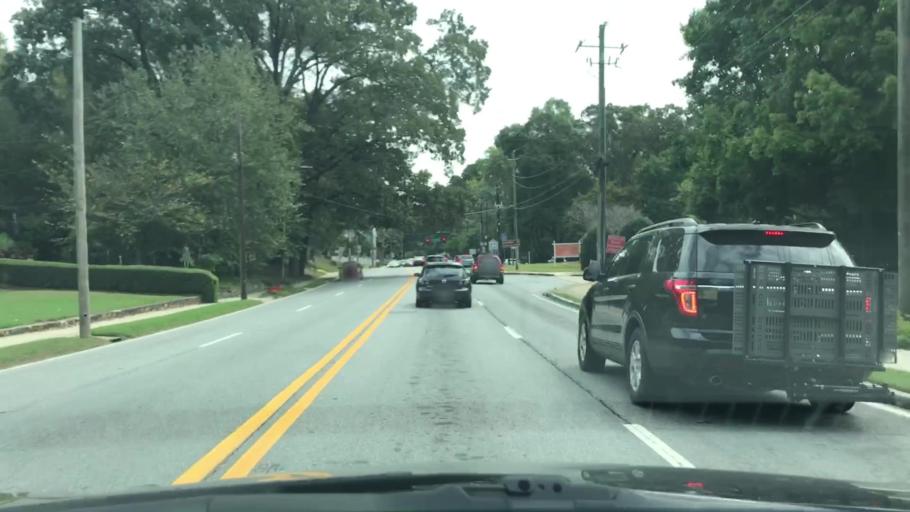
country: US
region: Georgia
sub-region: DeKalb County
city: North Decatur
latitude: 33.7859
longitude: -84.3054
